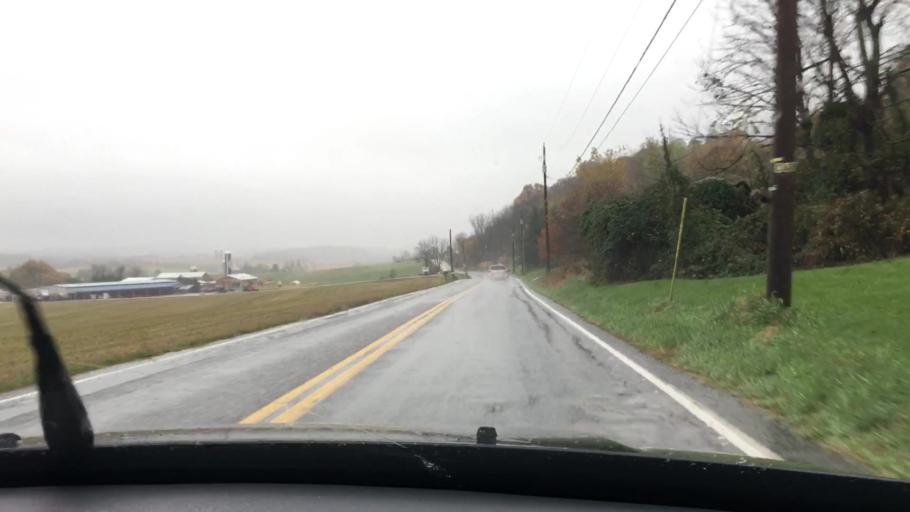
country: US
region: Pennsylvania
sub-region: York County
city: Glen Rock
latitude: 39.7403
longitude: -76.8155
